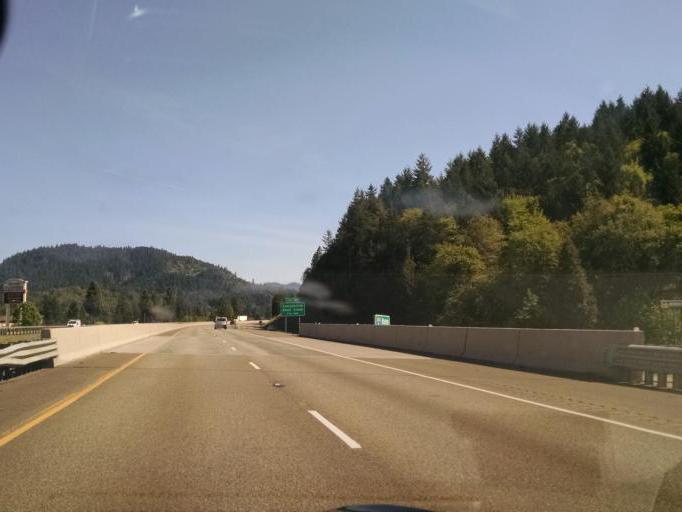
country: US
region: Oregon
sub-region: Douglas County
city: Canyonville
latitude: 42.9412
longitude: -123.2887
